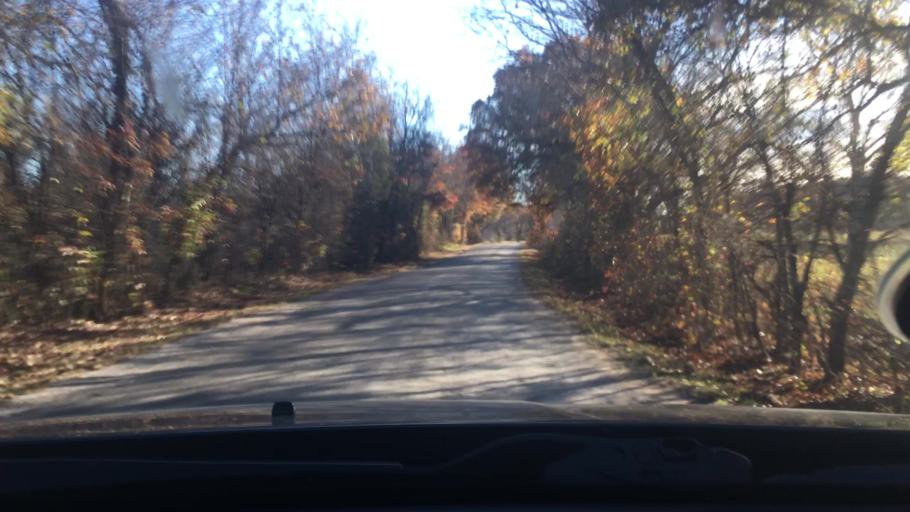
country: US
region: Oklahoma
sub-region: Murray County
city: Davis
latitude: 34.4879
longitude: -97.1573
